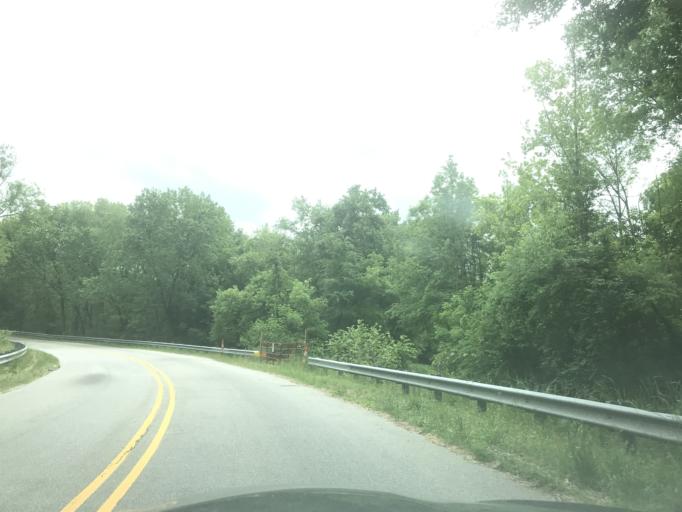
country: US
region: North Carolina
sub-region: Wake County
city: Raleigh
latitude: 35.8032
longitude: -78.5922
